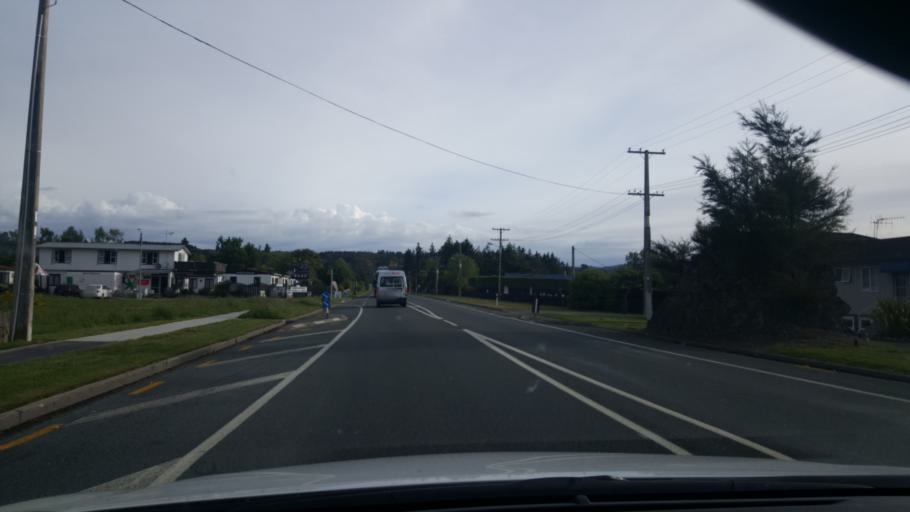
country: NZ
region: Waikato
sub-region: Taupo District
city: Taupo
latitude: -38.7900
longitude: 176.0763
